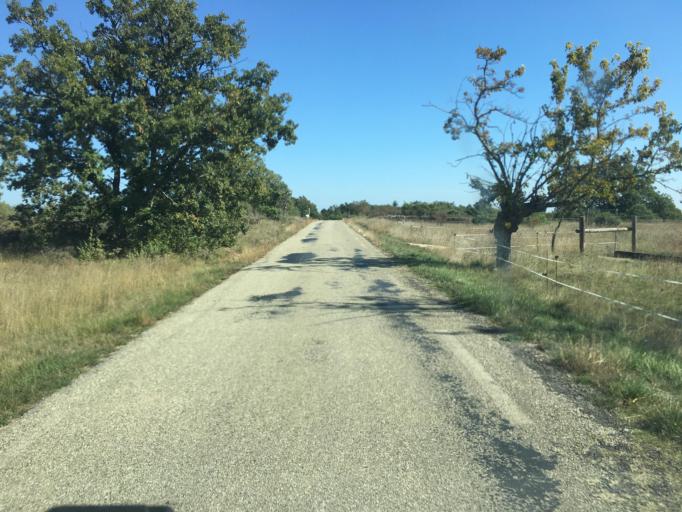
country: FR
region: Languedoc-Roussillon
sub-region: Departement du Gard
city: Barjac
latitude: 44.1681
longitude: 4.3211
